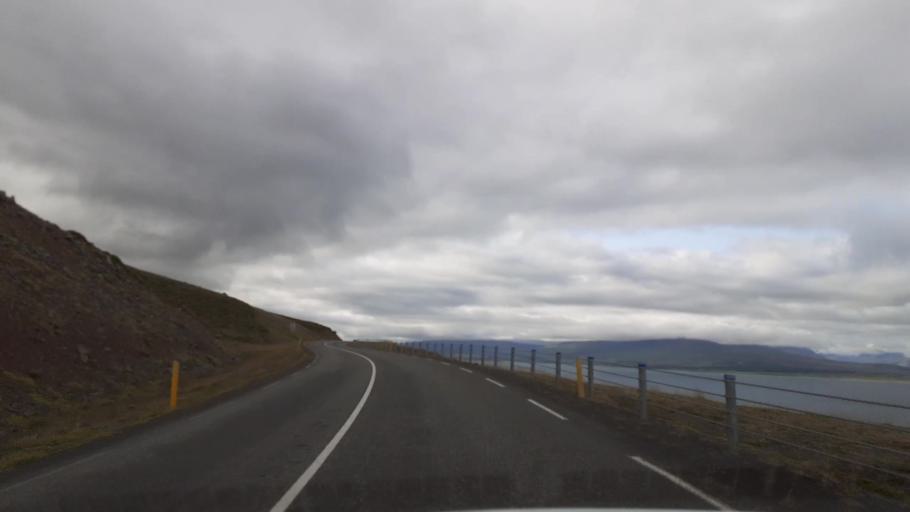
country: IS
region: Northeast
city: Akureyri
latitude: 65.8318
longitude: -18.0569
